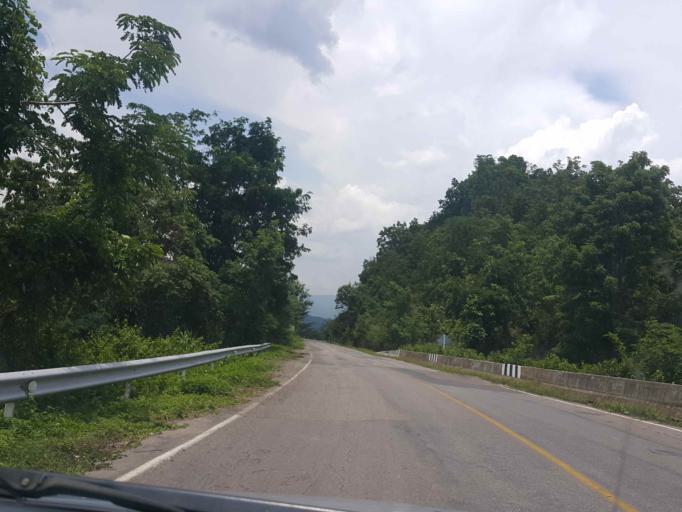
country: TH
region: Phayao
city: Chiang Muan
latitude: 18.9205
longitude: 100.2011
